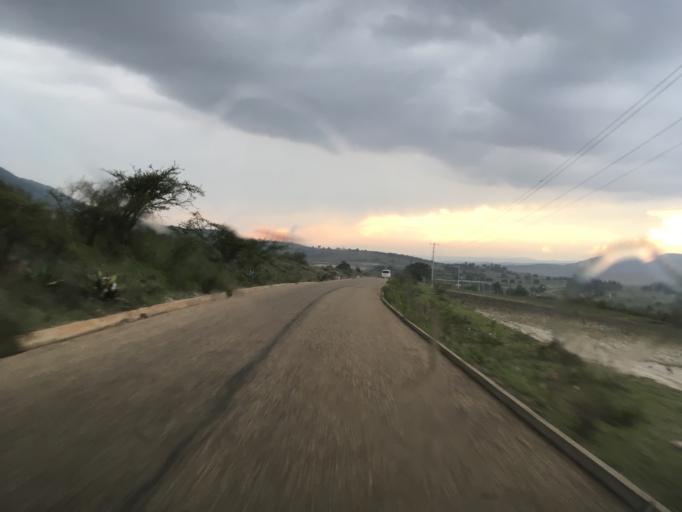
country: MX
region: Oaxaca
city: Santiago Tilantongo
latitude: 17.2803
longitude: -97.2909
